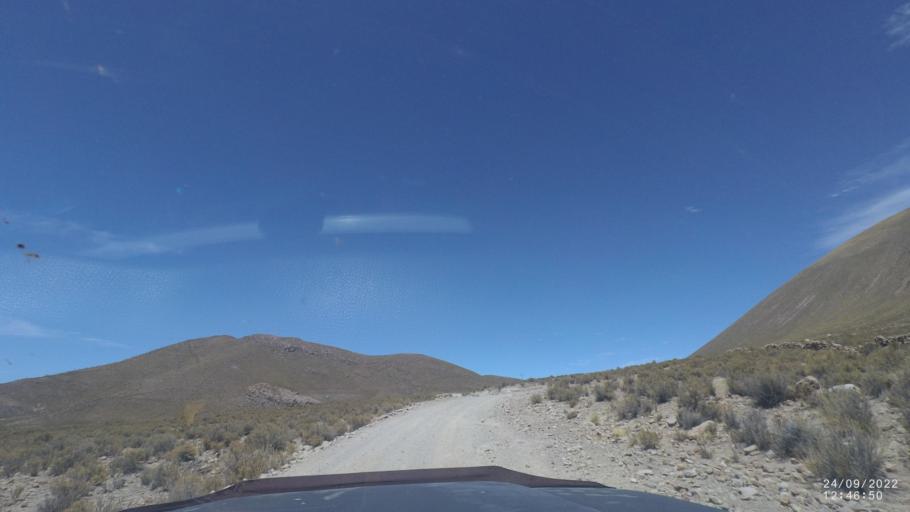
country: BO
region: Potosi
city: Colchani
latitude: -19.8058
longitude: -67.5699
